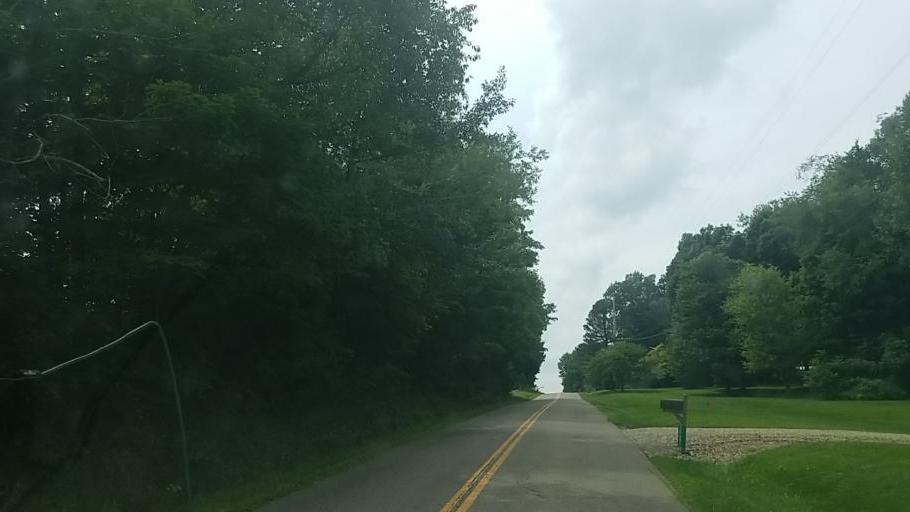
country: US
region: Ohio
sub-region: Knox County
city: Gambier
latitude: 40.3156
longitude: -82.3814
